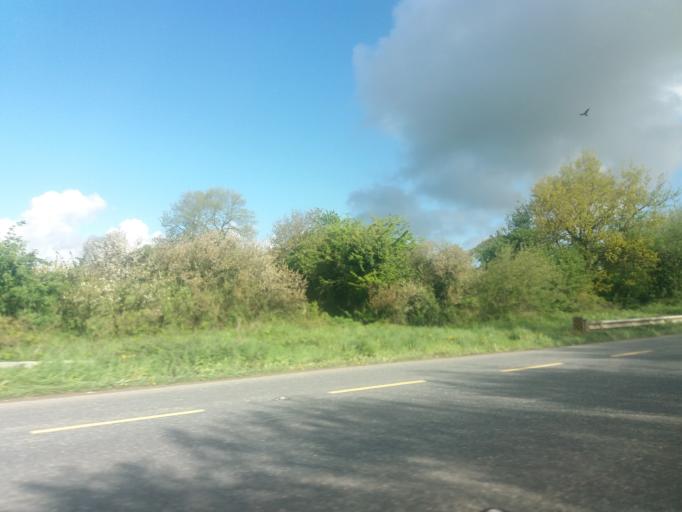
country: IE
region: Leinster
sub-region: Loch Garman
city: Enniscorthy
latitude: 52.5238
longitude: -6.5620
